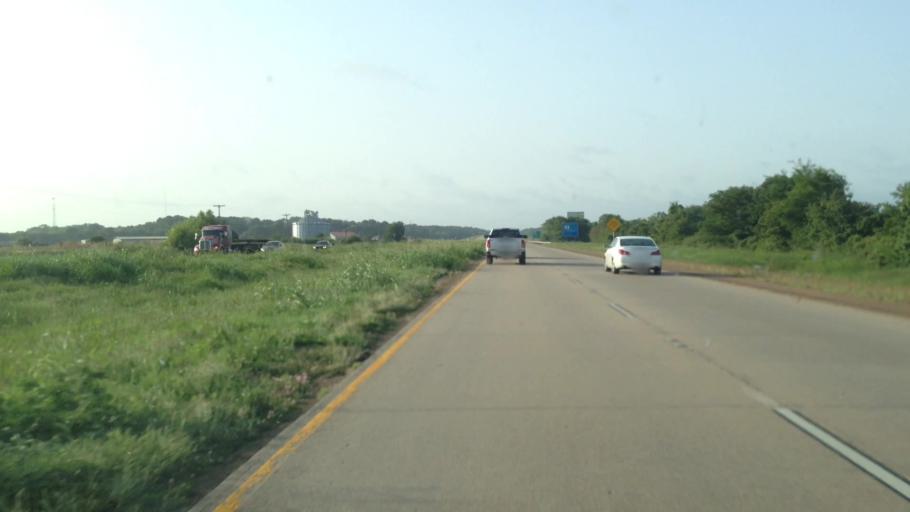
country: US
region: Louisiana
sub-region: Rapides Parish
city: Woodworth
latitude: 31.1750
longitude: -92.4657
